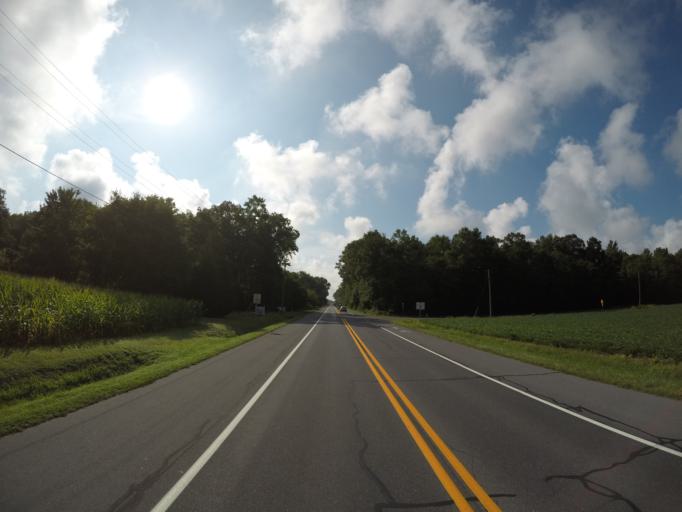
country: US
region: Delaware
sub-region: Sussex County
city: Bridgeville
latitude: 38.7649
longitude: -75.6446
